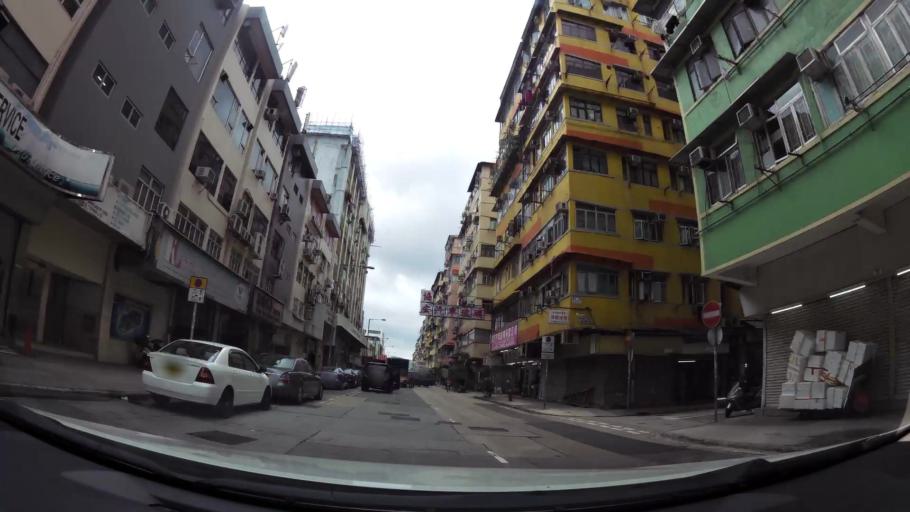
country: HK
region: Kowloon City
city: Kowloon
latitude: 22.3224
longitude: 114.1912
